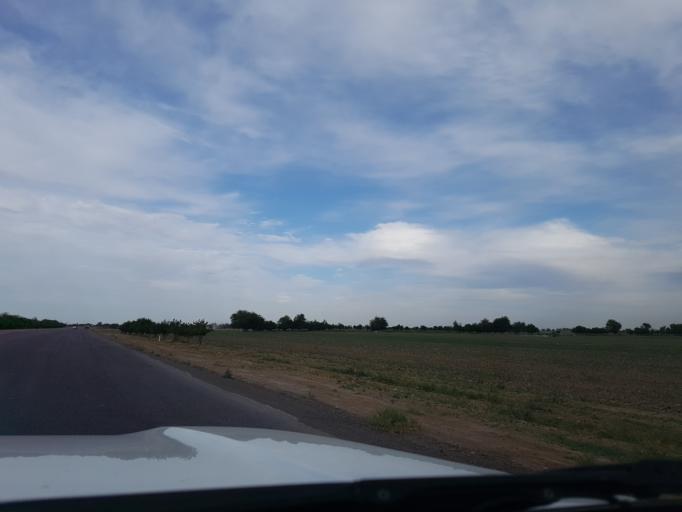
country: TM
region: Mary
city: Bayramaly
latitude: 37.6145
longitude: 62.2978
